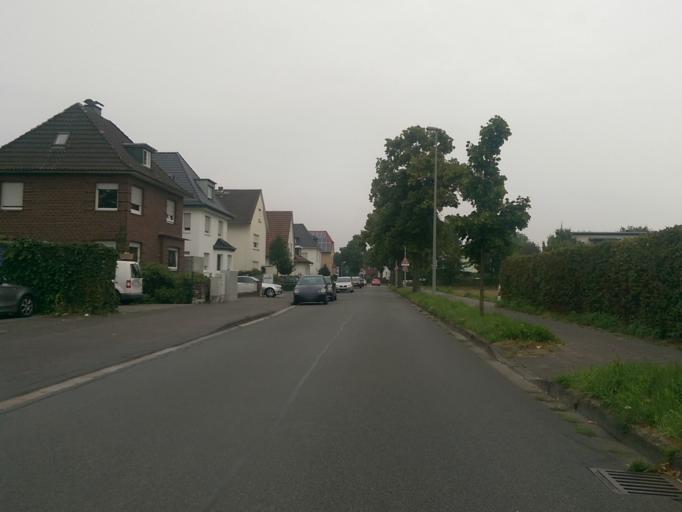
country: DE
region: North Rhine-Westphalia
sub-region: Regierungsbezirk Detmold
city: Guetersloh
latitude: 51.8958
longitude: 8.3754
